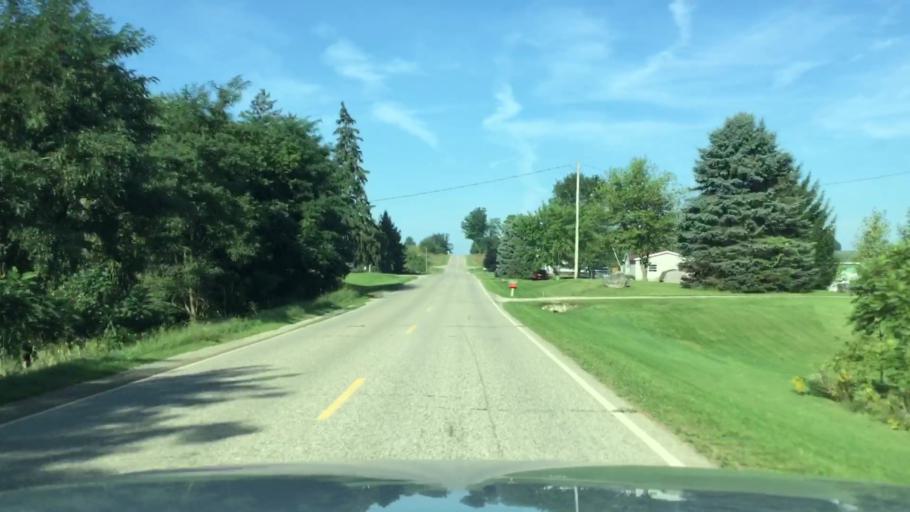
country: US
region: Michigan
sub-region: Lenawee County
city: Hudson
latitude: 41.9278
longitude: -84.3775
